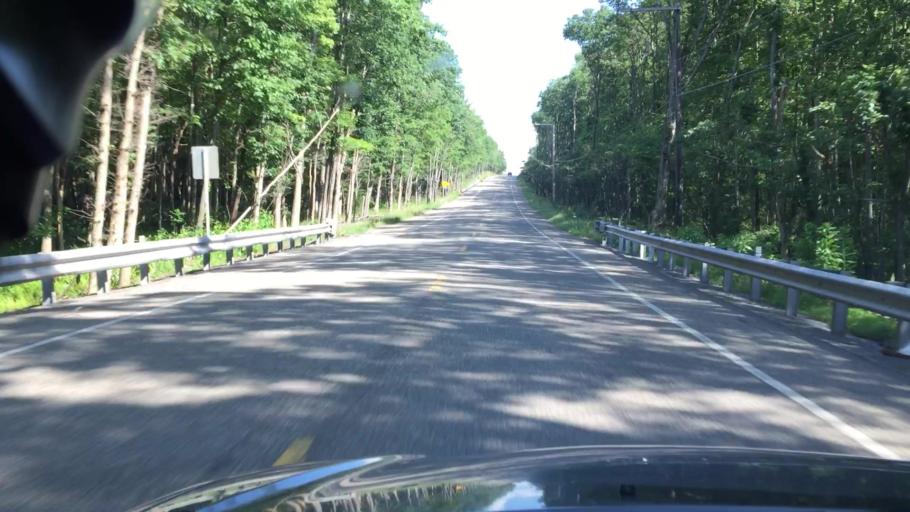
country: US
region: Pennsylvania
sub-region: Carbon County
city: Weatherly
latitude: 40.9072
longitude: -75.8266
